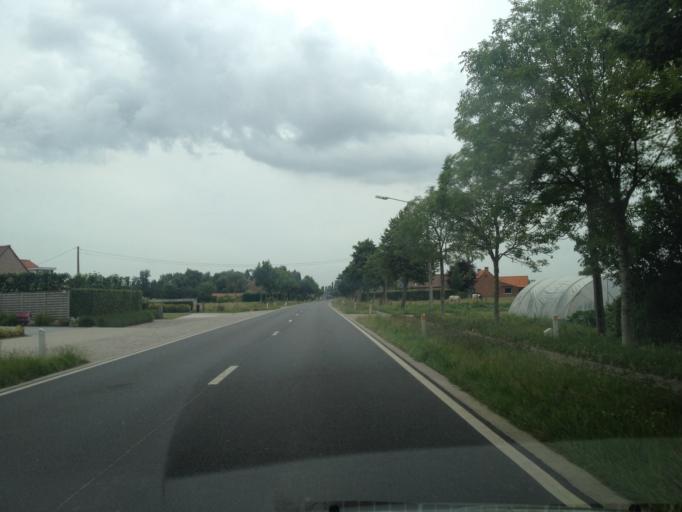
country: BE
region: Flanders
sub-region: Provincie West-Vlaanderen
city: Diksmuide
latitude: 50.9499
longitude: 2.8632
